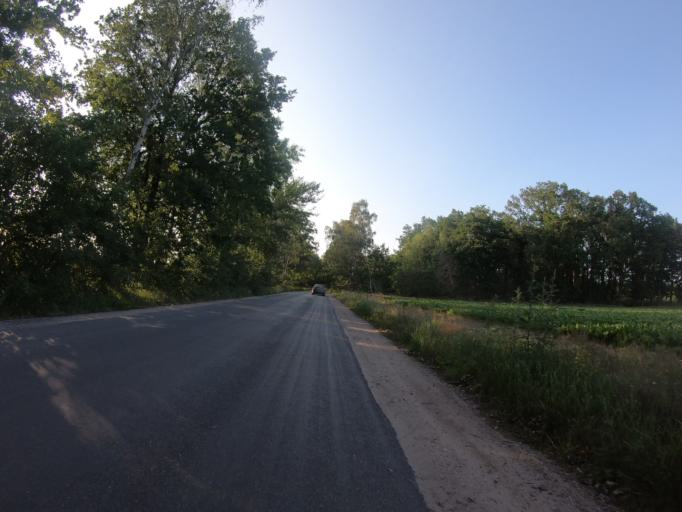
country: DE
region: Lower Saxony
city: Wagenhoff
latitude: 52.5165
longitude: 10.4802
